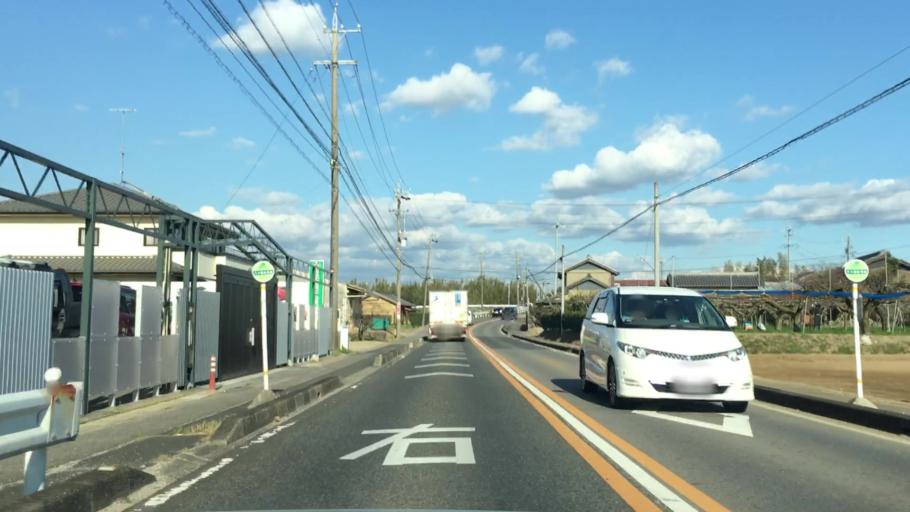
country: JP
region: Aichi
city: Nishio
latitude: 34.8727
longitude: 137.0772
